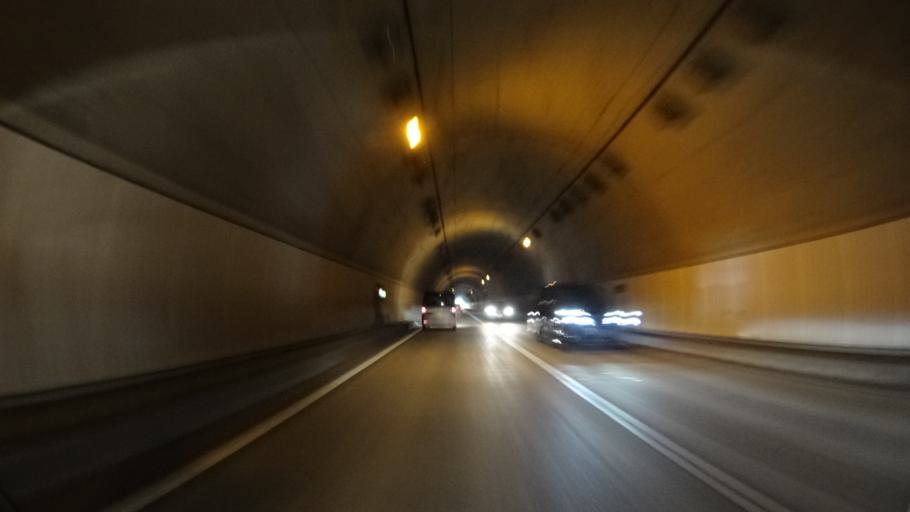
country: JP
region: Ehime
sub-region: Nishiuwa-gun
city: Ikata-cho
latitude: 33.5290
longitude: 132.3938
